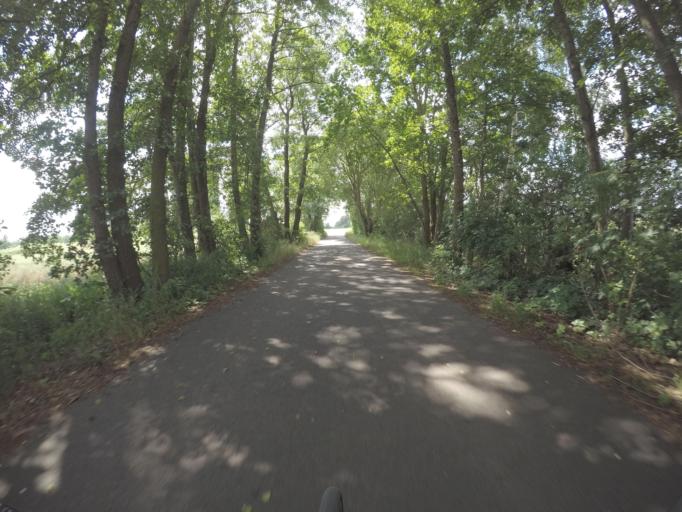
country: DE
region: Brandenburg
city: Roskow
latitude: 52.4500
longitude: 12.6777
